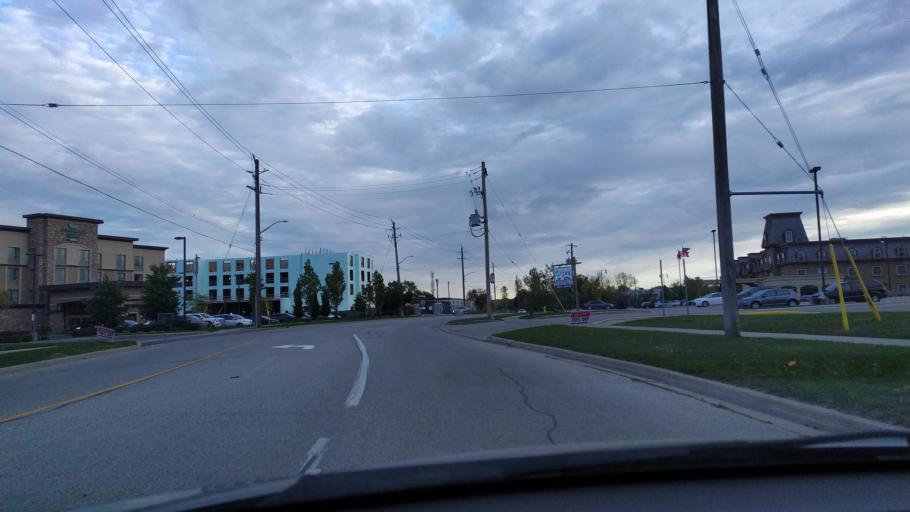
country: CA
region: Ontario
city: Waterloo
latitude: 43.5079
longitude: -80.5552
